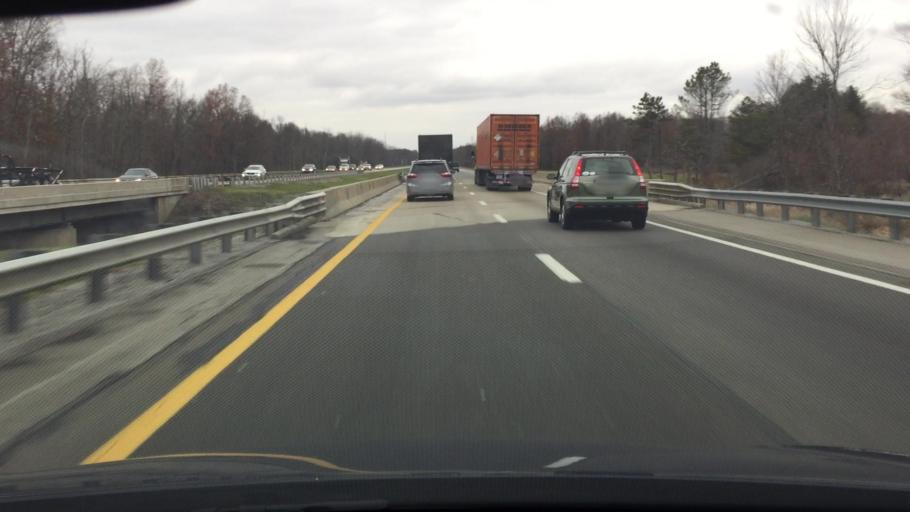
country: US
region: Ohio
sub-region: Mahoning County
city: Boardman
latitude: 40.9919
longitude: -80.6911
